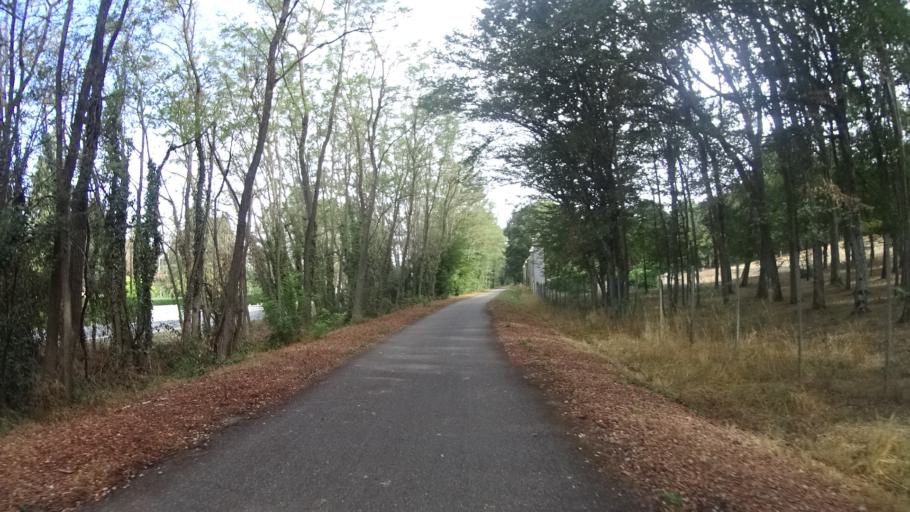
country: FR
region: Auvergne
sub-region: Departement de l'Allier
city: Diou
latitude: 46.5736
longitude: 3.7457
